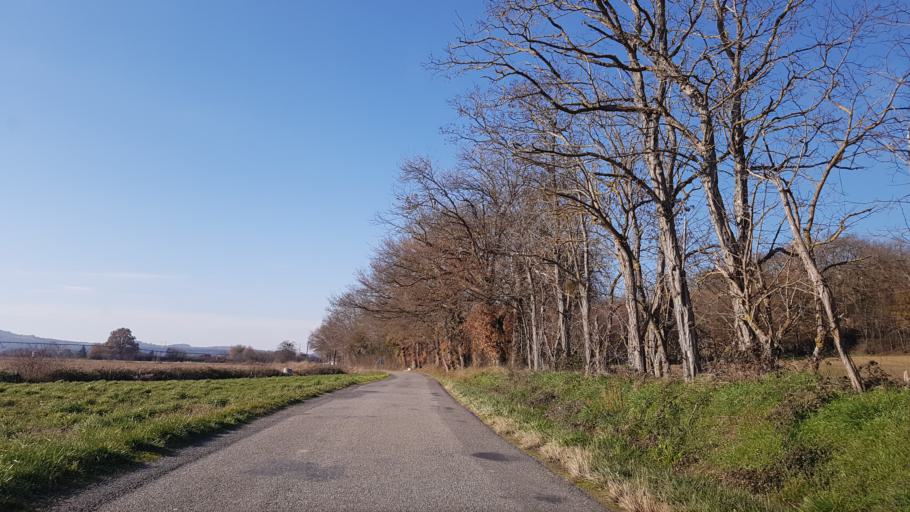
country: FR
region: Midi-Pyrenees
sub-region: Departement de l'Ariege
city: Mazeres
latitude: 43.1836
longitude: 1.6454
